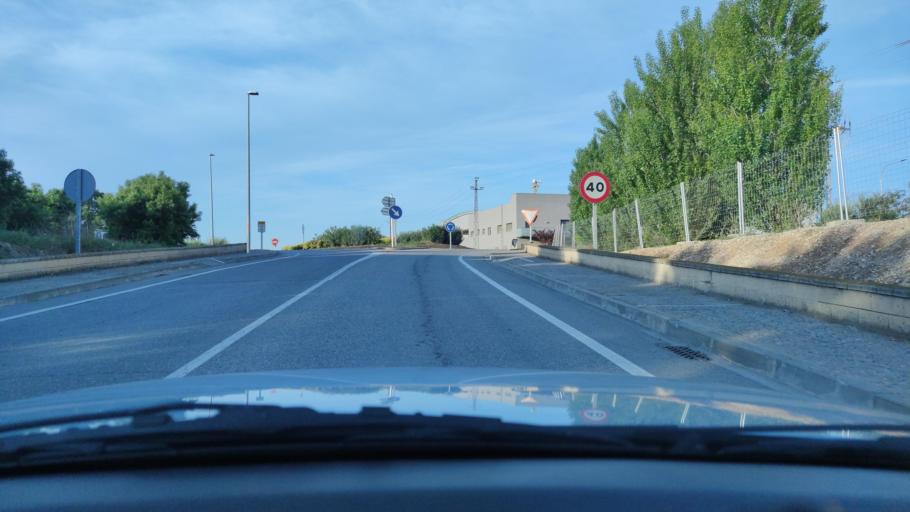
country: ES
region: Catalonia
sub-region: Provincia de Lleida
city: Bellpuig
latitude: 41.6329
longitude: 1.0047
